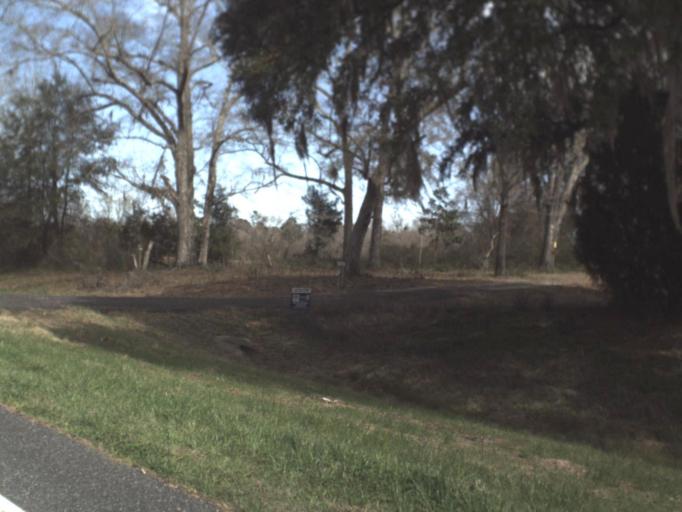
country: US
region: Florida
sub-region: Jackson County
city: Marianna
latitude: 30.7702
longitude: -85.3741
